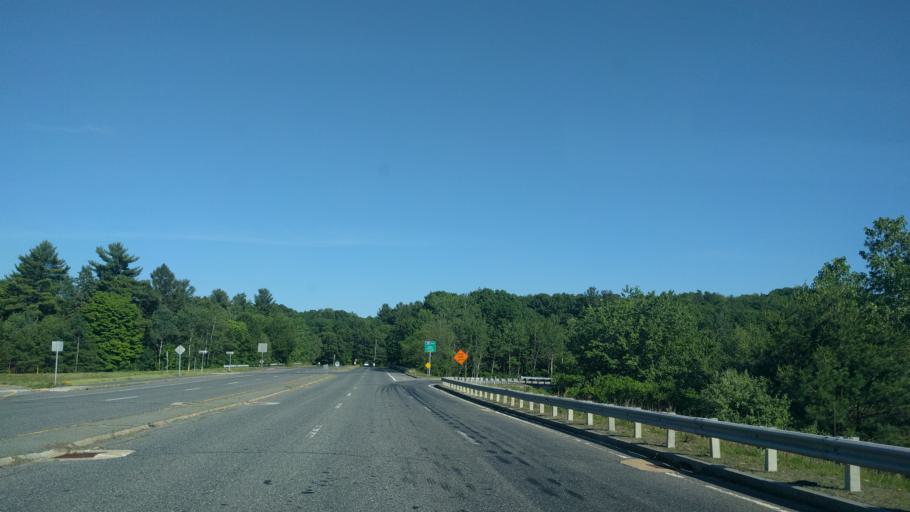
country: US
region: Massachusetts
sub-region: Worcester County
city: Oxford
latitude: 42.1504
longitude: -71.8560
